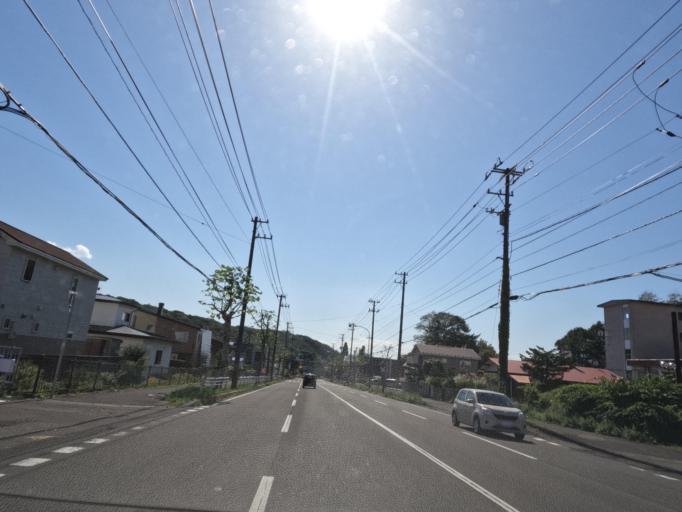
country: JP
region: Hokkaido
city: Muroran
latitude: 42.3693
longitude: 141.0270
